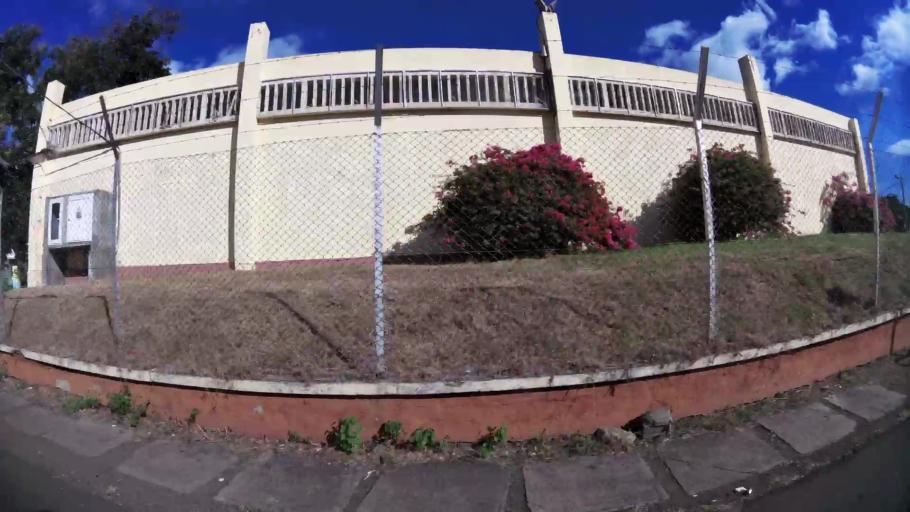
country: MU
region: Pamplemousses
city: Le Hochet
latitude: -20.1522
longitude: 57.5146
